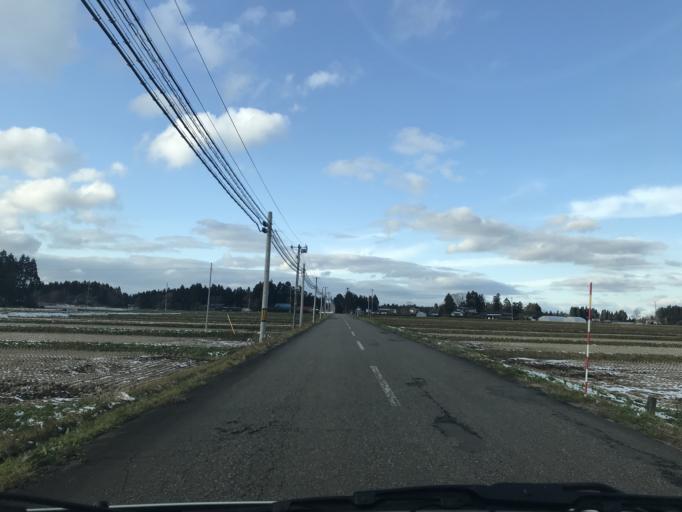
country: JP
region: Iwate
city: Kitakami
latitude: 39.2145
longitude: 141.0487
